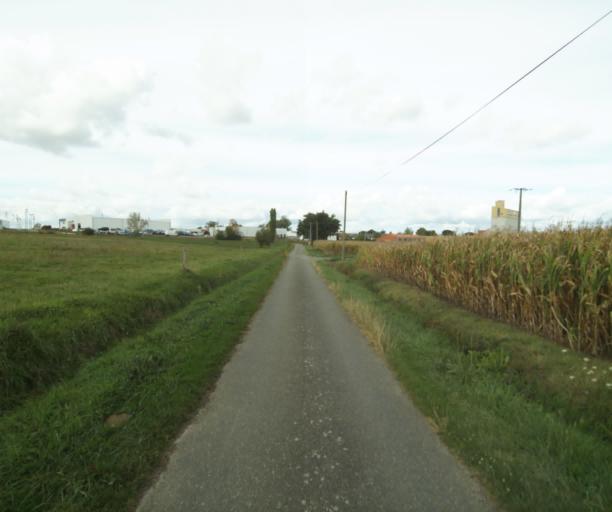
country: FR
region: Midi-Pyrenees
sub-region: Departement du Gers
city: Eauze
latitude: 43.8390
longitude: 0.0957
